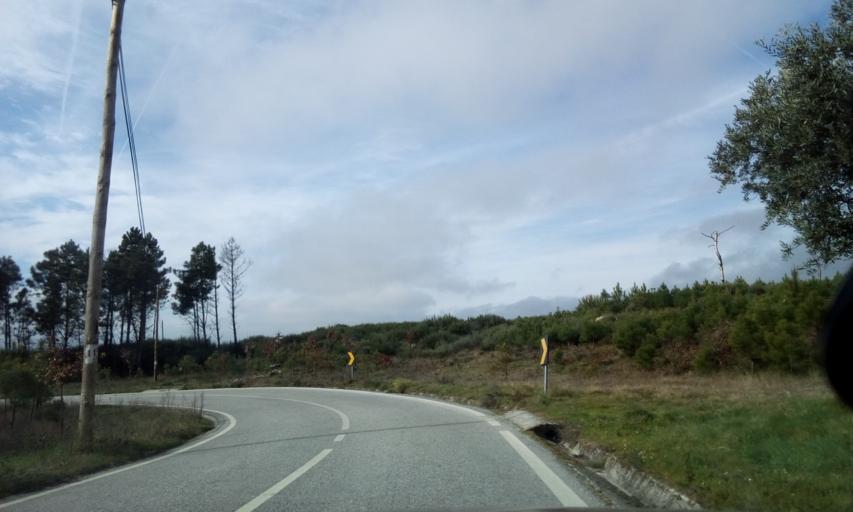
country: PT
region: Guarda
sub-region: Aguiar da Beira
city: Aguiar da Beira
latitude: 40.7545
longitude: -7.5440
